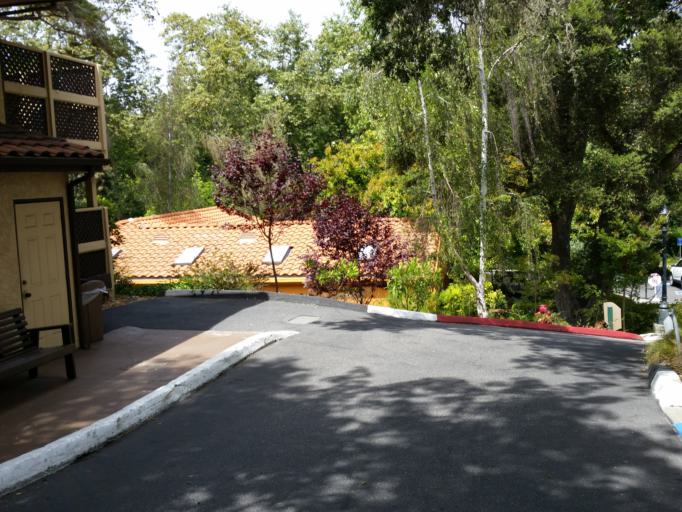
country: US
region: California
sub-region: San Luis Obispo County
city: Avila Beach
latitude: 35.1862
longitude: -120.7139
